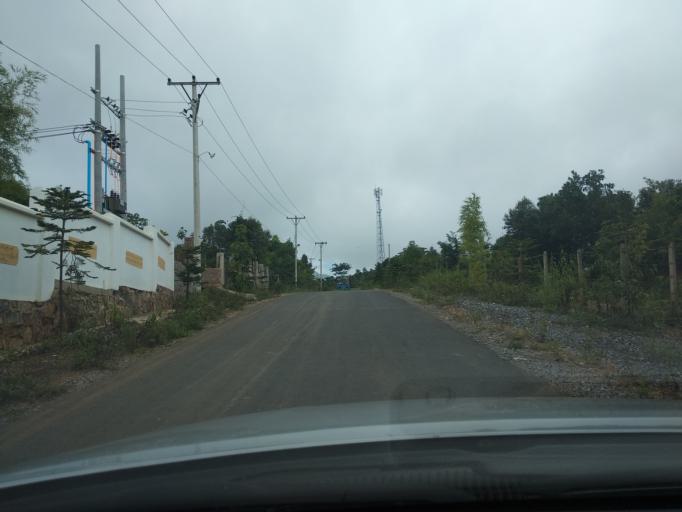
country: MM
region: Mandalay
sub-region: Pyin Oo Lwin District
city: Pyin Oo Lwin
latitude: 21.9220
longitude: 96.3767
